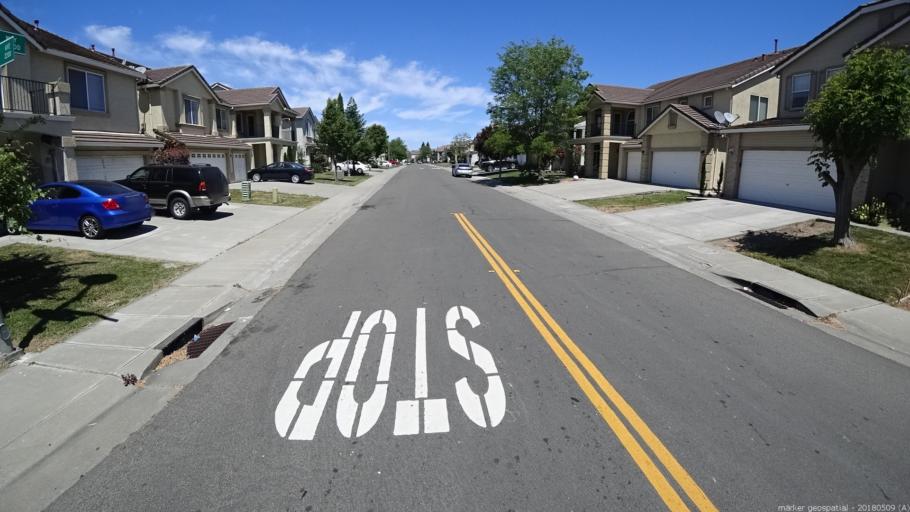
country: US
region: California
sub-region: Sacramento County
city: Sacramento
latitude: 38.6334
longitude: -121.5117
